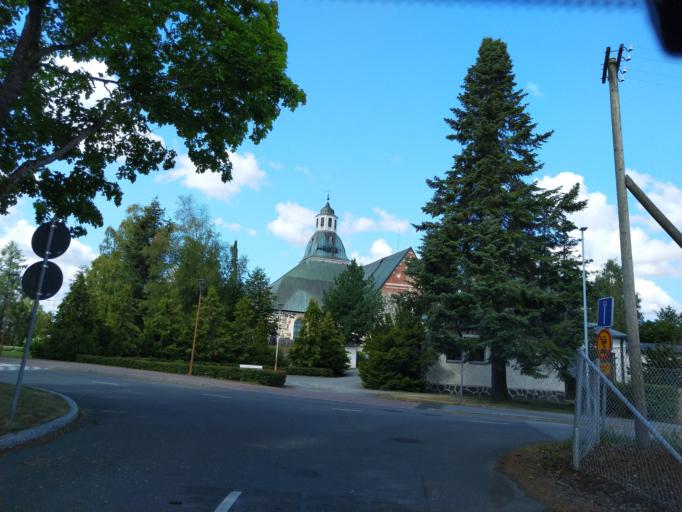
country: FI
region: Satakunta
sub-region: Pori
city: Huittinen
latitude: 61.1803
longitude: 22.6948
